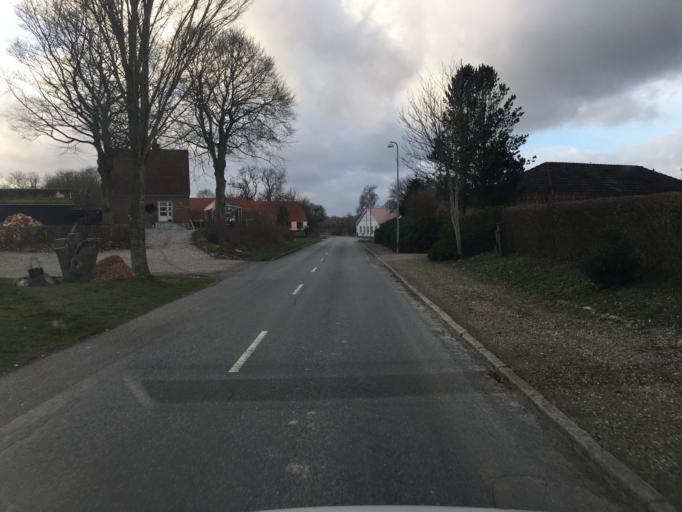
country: DK
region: South Denmark
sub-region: Sonderborg Kommune
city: Grasten
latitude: 54.9703
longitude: 9.5179
